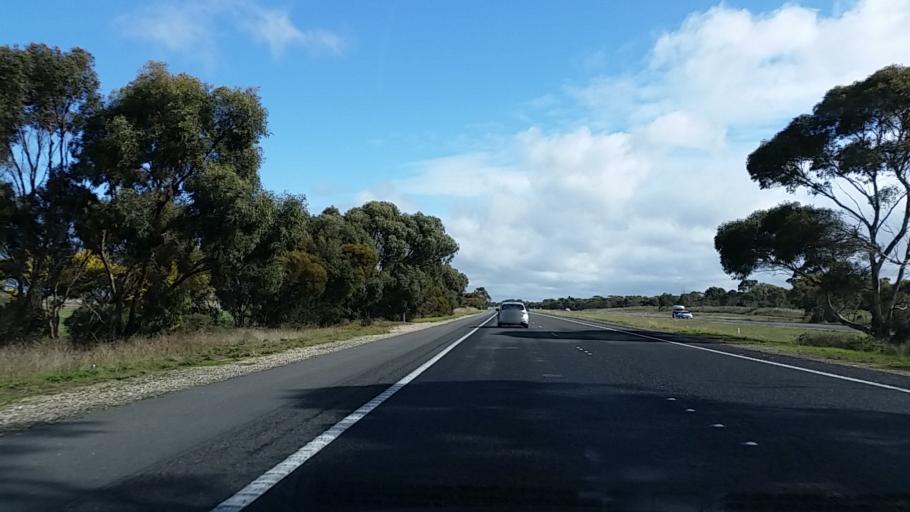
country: AU
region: South Australia
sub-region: Mount Barker
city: Callington
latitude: -35.1308
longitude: 139.0912
